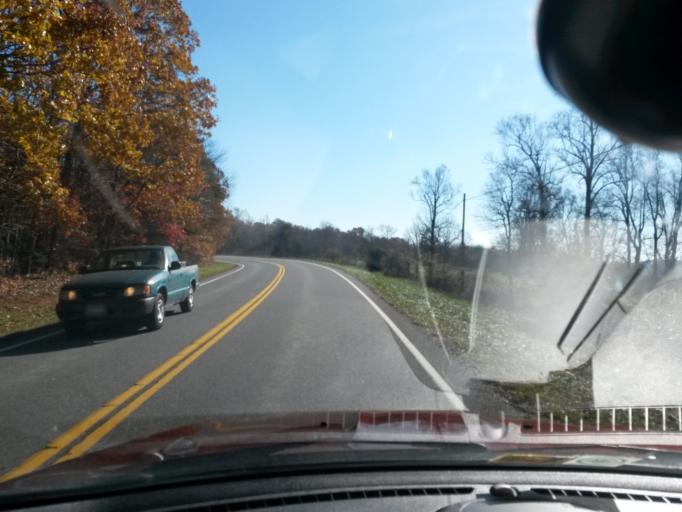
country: US
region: Virginia
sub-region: City of Bedford
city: Bedford
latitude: 37.4088
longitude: -79.5622
